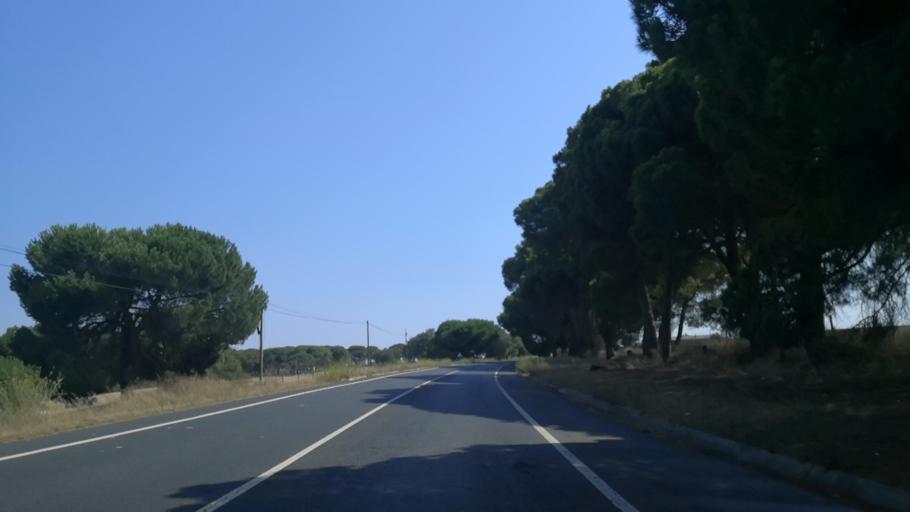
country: PT
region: Evora
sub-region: Vendas Novas
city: Vendas Novas
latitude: 38.6999
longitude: -8.6115
